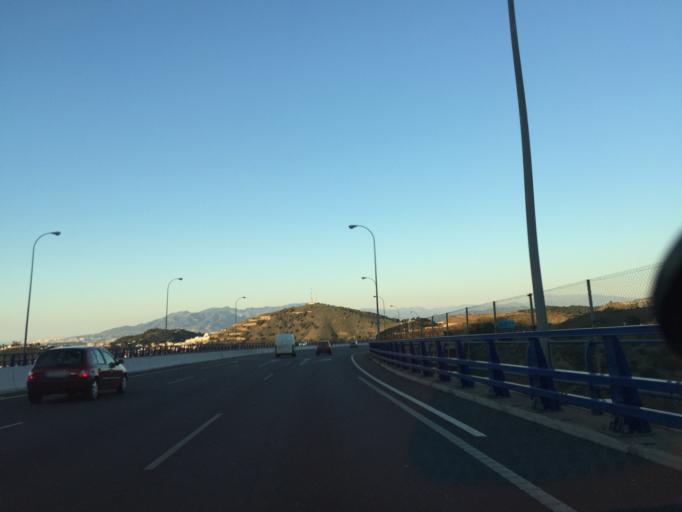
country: ES
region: Andalusia
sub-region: Provincia de Malaga
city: Malaga
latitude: 36.7394
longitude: -4.3890
